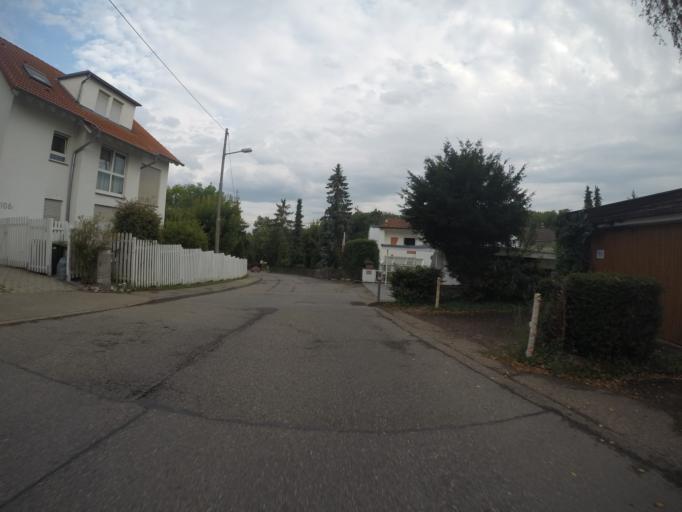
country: DE
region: Baden-Wuerttemberg
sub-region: Regierungsbezirk Stuttgart
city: Ostfildern
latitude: 48.7305
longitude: 9.2039
